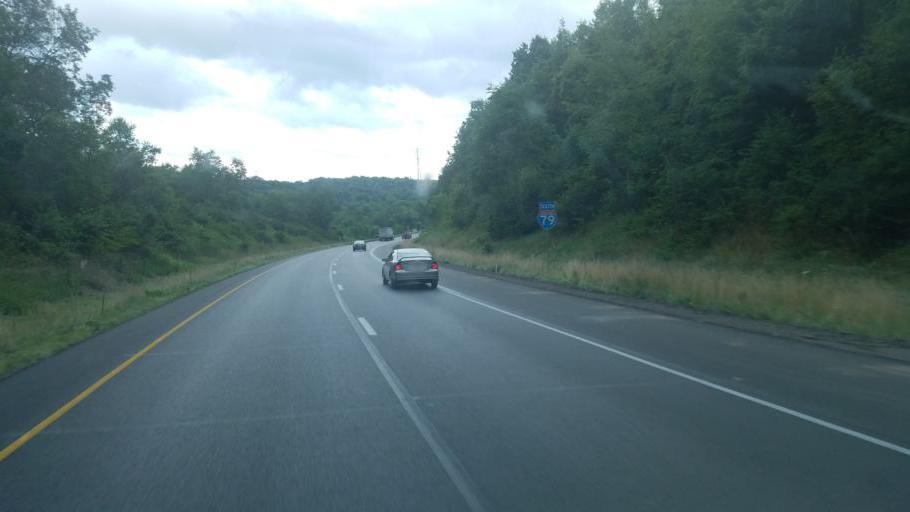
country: US
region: Pennsylvania
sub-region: Butler County
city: Evans City
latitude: 40.7518
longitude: -80.1085
